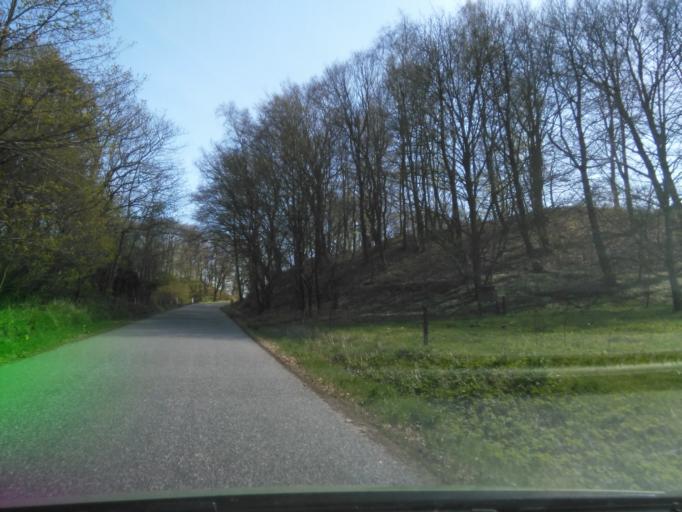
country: DK
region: Central Jutland
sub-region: Viborg Kommune
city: Viborg
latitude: 56.3611
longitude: 9.3387
